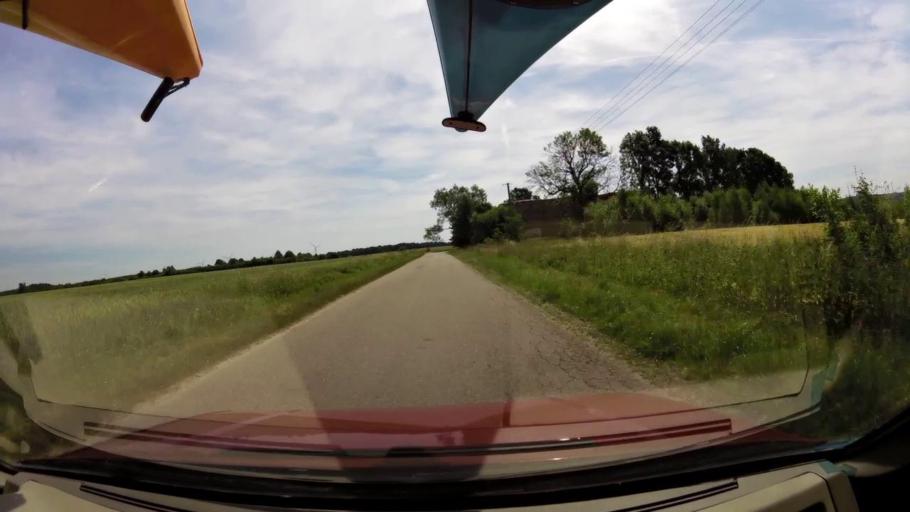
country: PL
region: West Pomeranian Voivodeship
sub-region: Powiat slawienski
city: Darlowo
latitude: 54.3150
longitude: 16.4205
